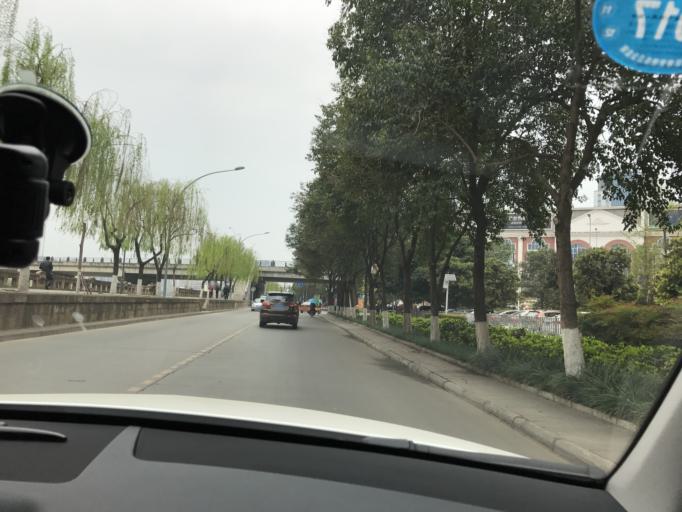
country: CN
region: Sichuan
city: Mianyang
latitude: 31.4546
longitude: 104.7084
